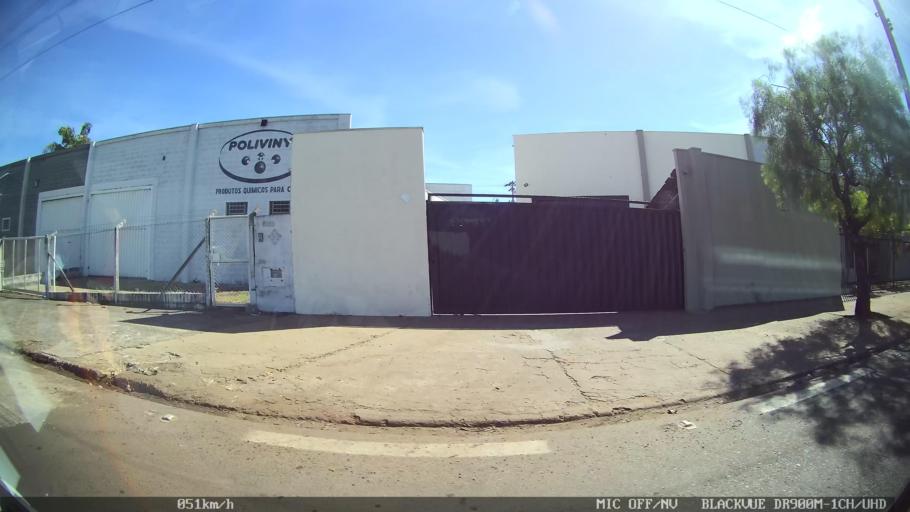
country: BR
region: Sao Paulo
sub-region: Franca
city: Franca
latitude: -20.5558
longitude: -47.4399
